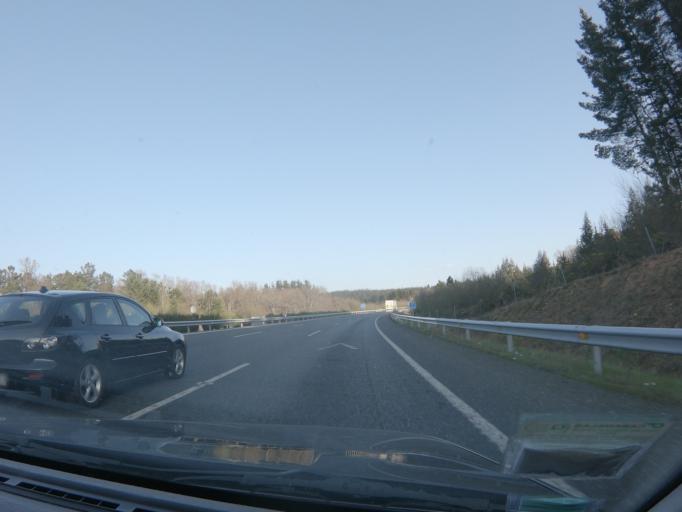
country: ES
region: Galicia
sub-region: Provincia de Lugo
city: O Paramo
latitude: 42.9311
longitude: -7.3647
